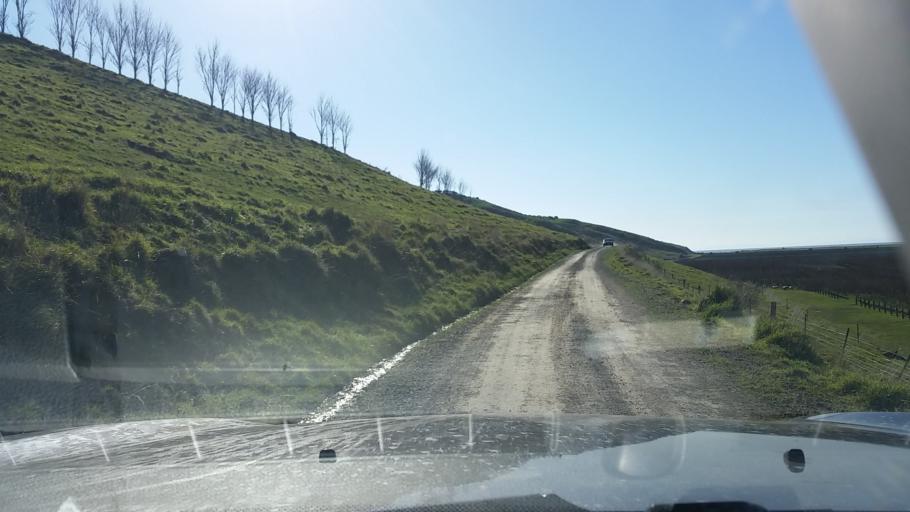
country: NZ
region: Marlborough
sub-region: Marlborough District
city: Blenheim
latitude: -41.6683
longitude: 174.1402
